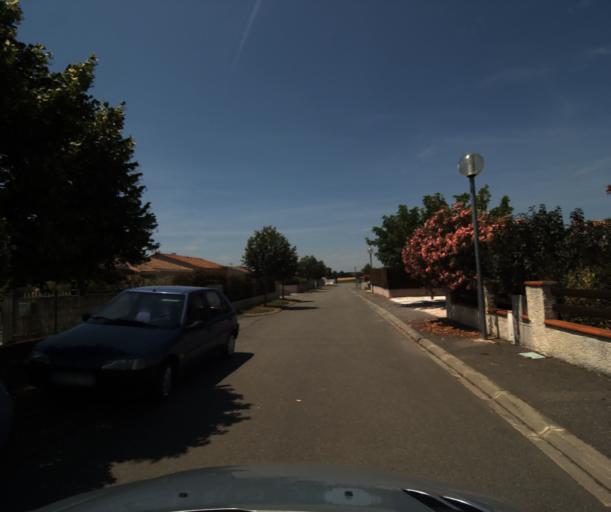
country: FR
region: Midi-Pyrenees
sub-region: Departement de la Haute-Garonne
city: Labastidette
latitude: 43.4649
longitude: 1.2472
